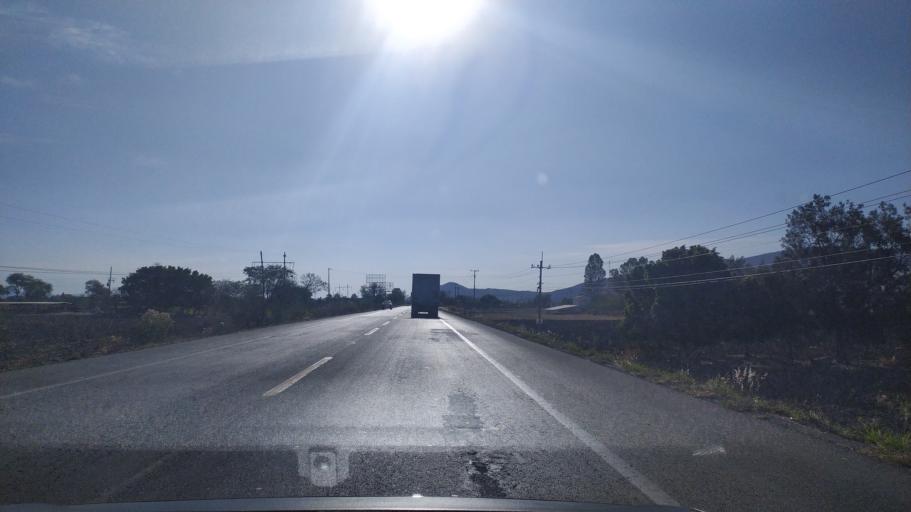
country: MX
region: Jalisco
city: Jamay
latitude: 20.2937
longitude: -102.6517
